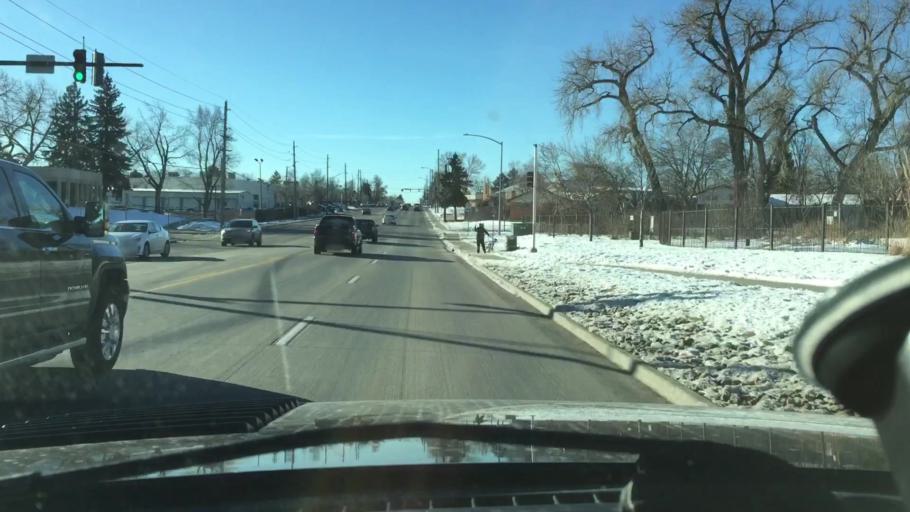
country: US
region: Colorado
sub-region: Adams County
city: Northglenn
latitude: 39.8881
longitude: -104.9968
